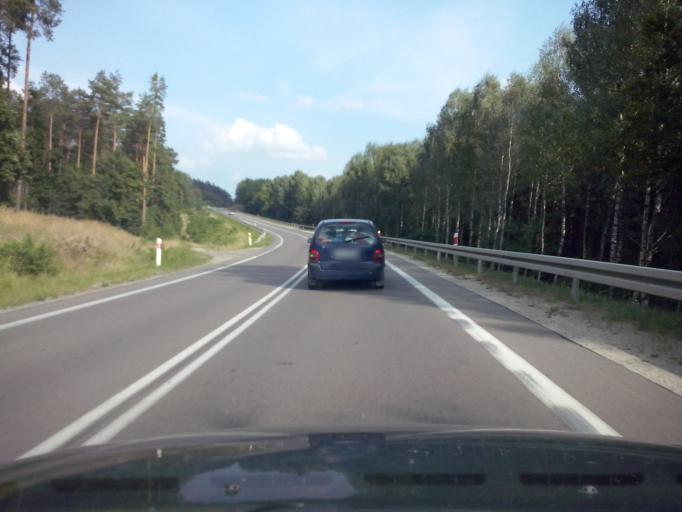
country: PL
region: Subcarpathian Voivodeship
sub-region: Powiat mielecki
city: Przeclaw
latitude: 50.2747
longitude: 21.5279
